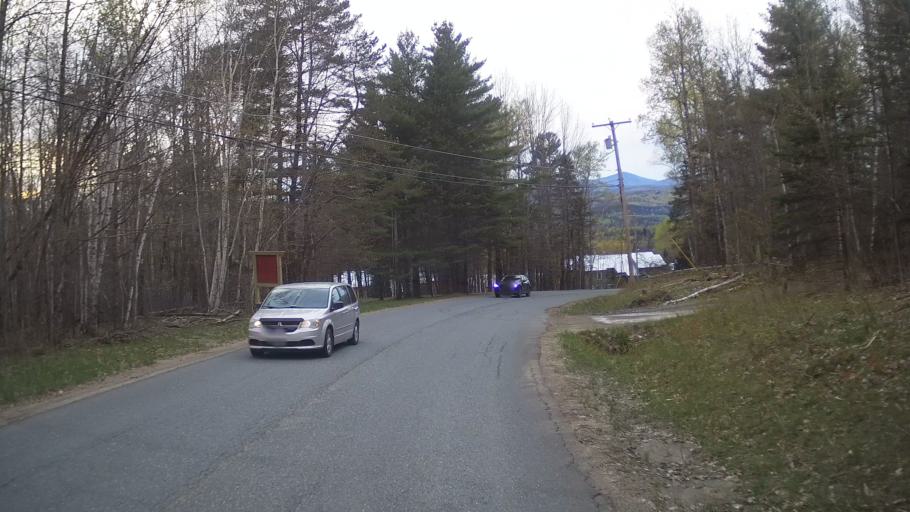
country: US
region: Vermont
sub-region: Caledonia County
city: Lyndonville
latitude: 44.5877
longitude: -71.9024
